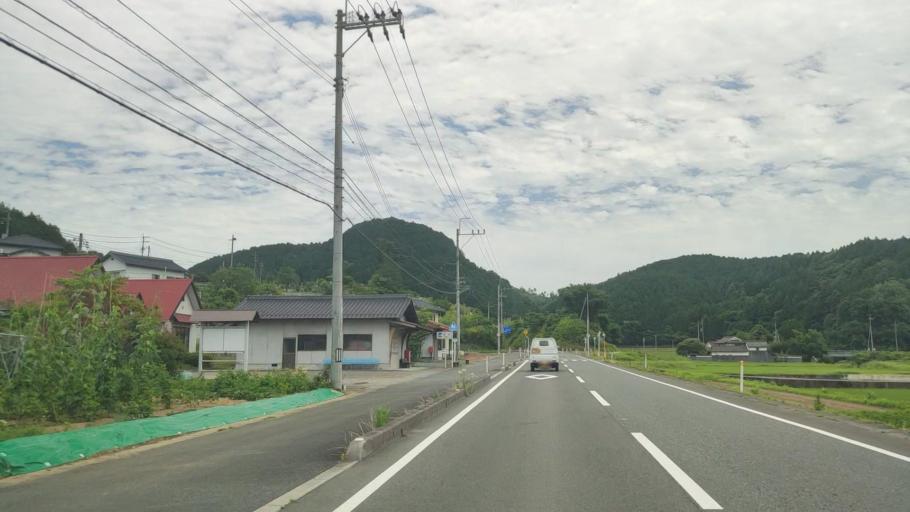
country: JP
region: Okayama
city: Tsuyama
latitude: 35.0627
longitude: 134.2119
